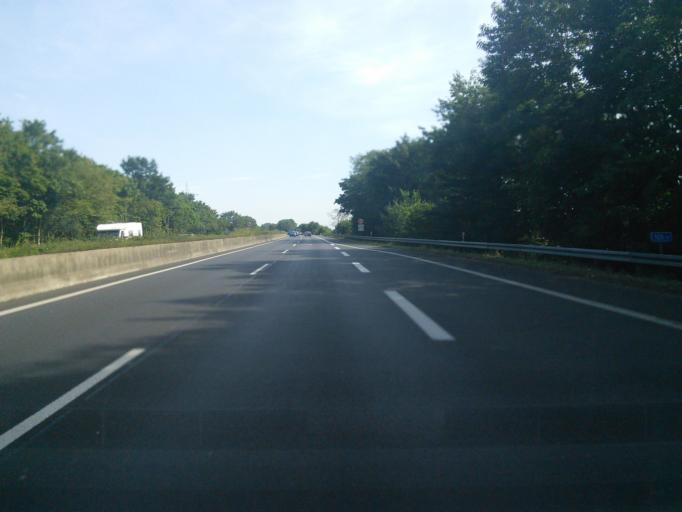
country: DE
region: North Rhine-Westphalia
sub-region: Regierungsbezirk Koln
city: Sinnersdorf
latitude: 51.0391
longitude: 6.8374
